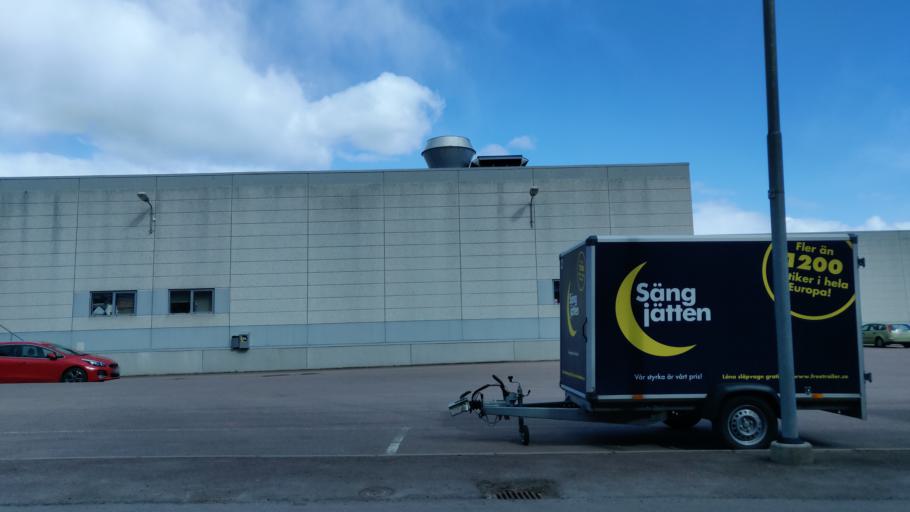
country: SE
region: Vaermland
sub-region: Hammaro Kommun
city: Skoghall
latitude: 59.3751
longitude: 13.4382
